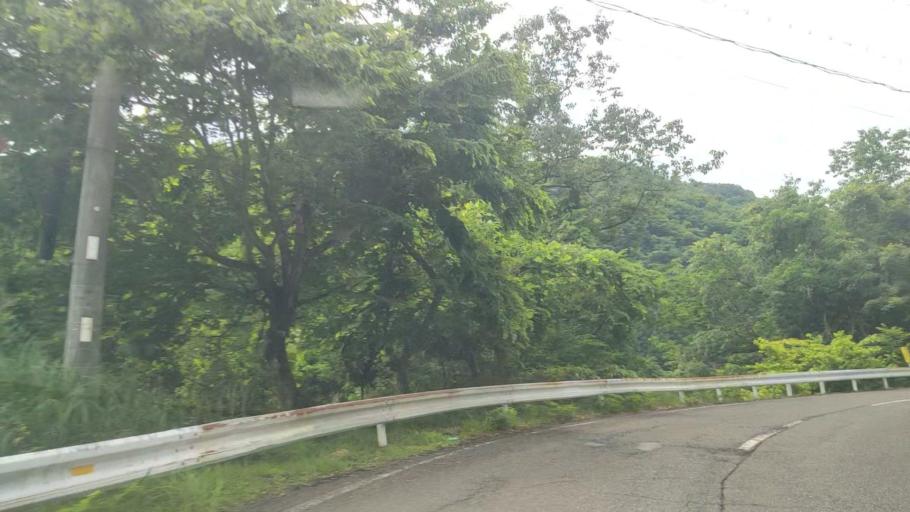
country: JP
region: Hyogo
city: Toyooka
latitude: 35.5199
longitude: 134.6943
